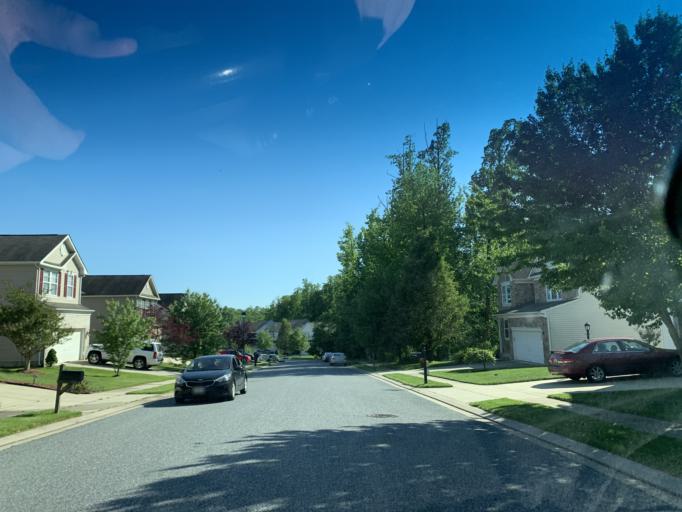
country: US
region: Maryland
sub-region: Harford County
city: Riverside
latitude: 39.4834
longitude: -76.2389
